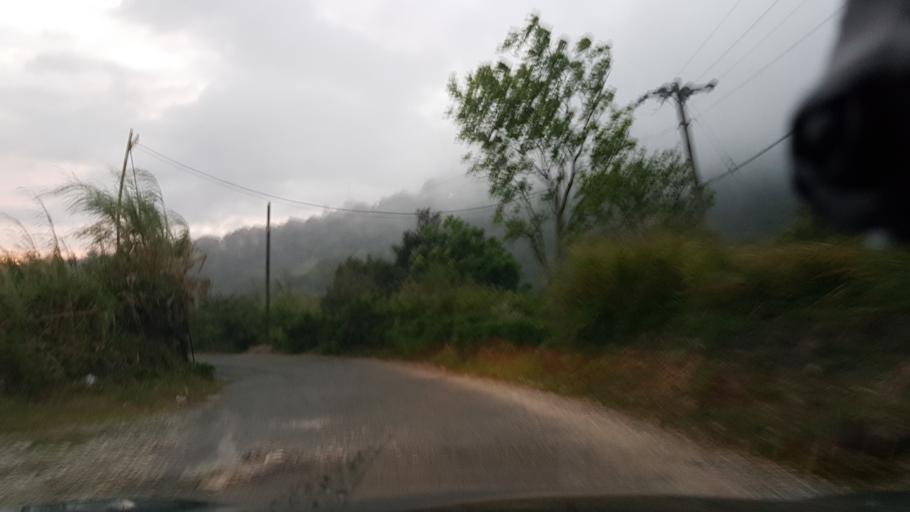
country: JM
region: Saint Andrew
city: Gordon Town
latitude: 18.0700
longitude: -76.7073
